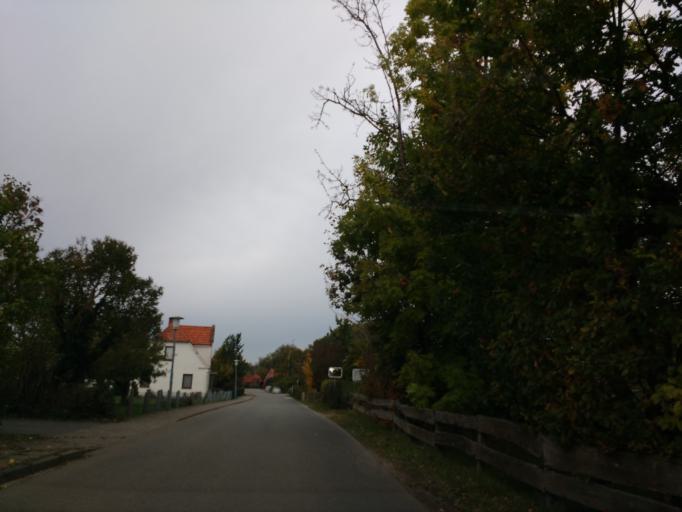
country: DE
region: Schleswig-Holstein
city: Grube
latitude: 54.2036
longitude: 11.0208
